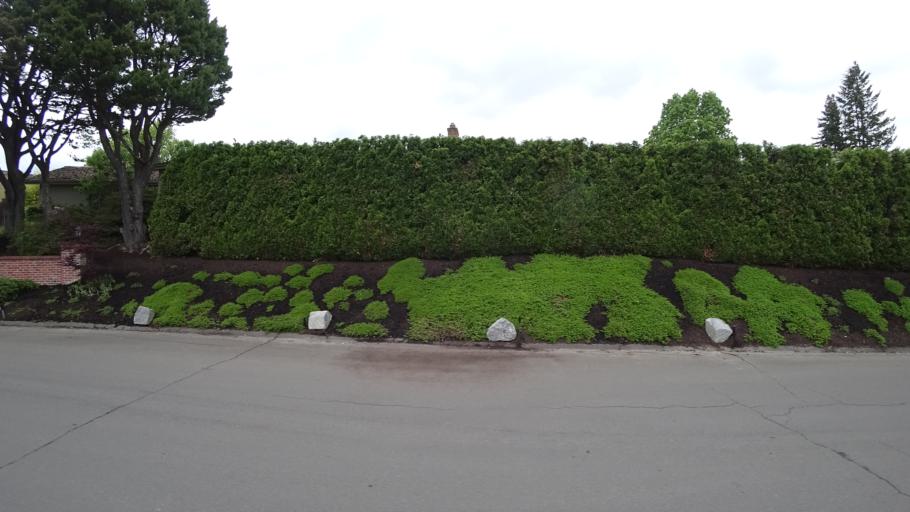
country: US
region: Oregon
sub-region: Washington County
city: Raleigh Hills
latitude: 45.4814
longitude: -122.7556
